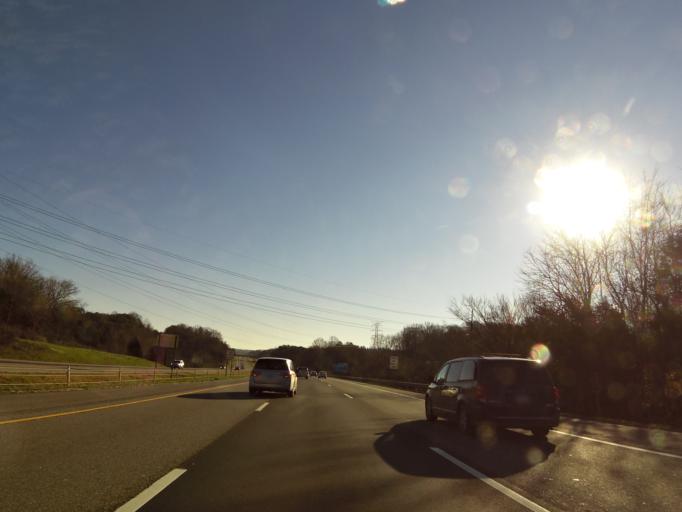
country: US
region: Tennessee
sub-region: Knox County
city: Mascot
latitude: 36.0077
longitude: -83.8136
